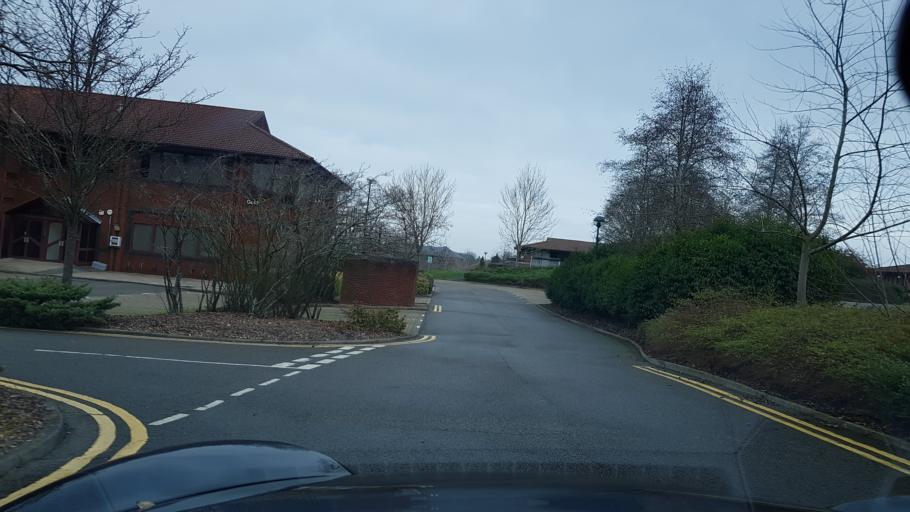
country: GB
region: England
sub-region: Surrey
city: Guildford
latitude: 51.2397
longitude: -0.6156
